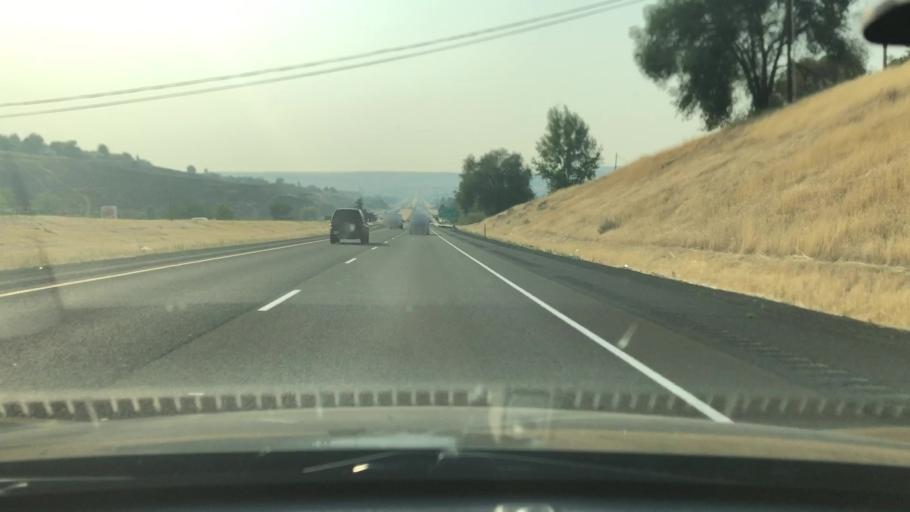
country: US
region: Oregon
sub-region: Umatilla County
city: Pendleton
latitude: 45.6624
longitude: -118.8036
